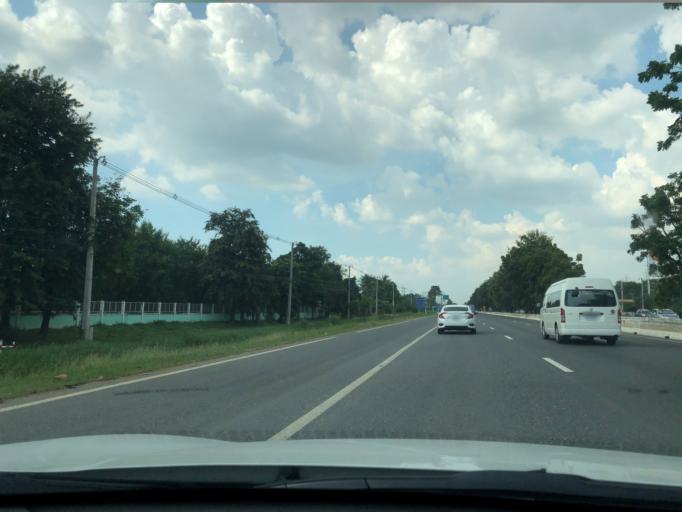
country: TH
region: Nakhon Sawan
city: Krok Phra
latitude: 15.5833
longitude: 100.1242
